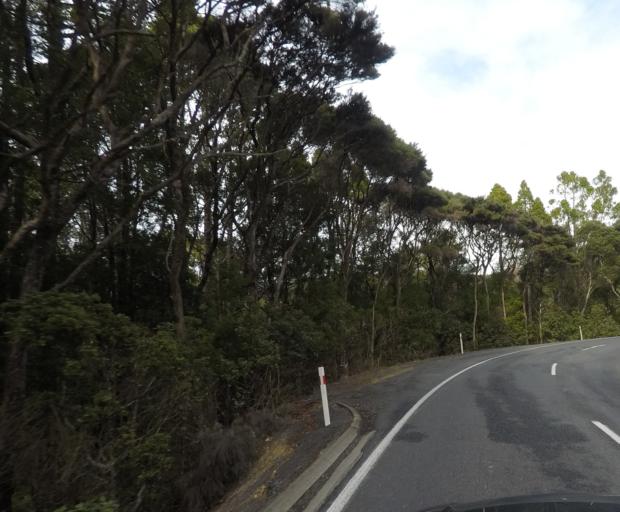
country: NZ
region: Northland
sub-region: Whangarei
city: Ruakaka
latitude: -36.0605
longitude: 174.5687
